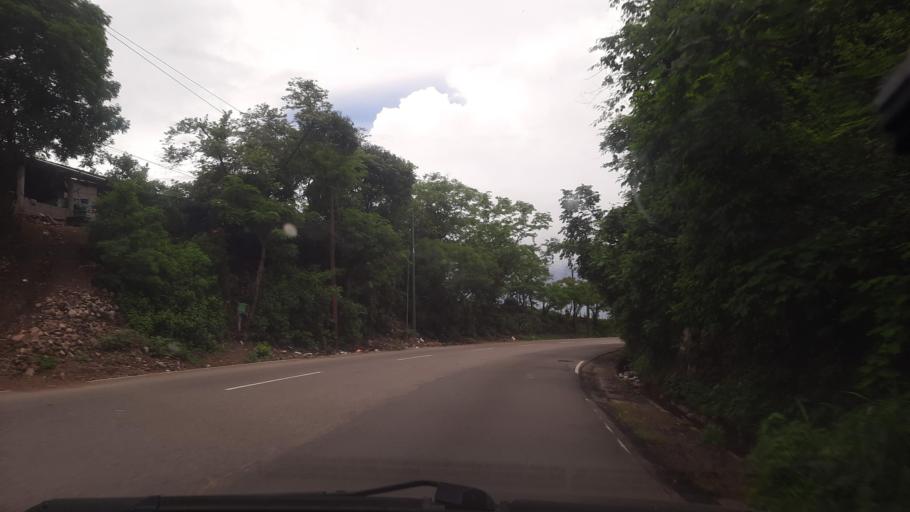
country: GT
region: Chiquimula
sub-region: Municipio de Chiquimula
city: Chiquimula
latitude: 14.8636
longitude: -89.5094
